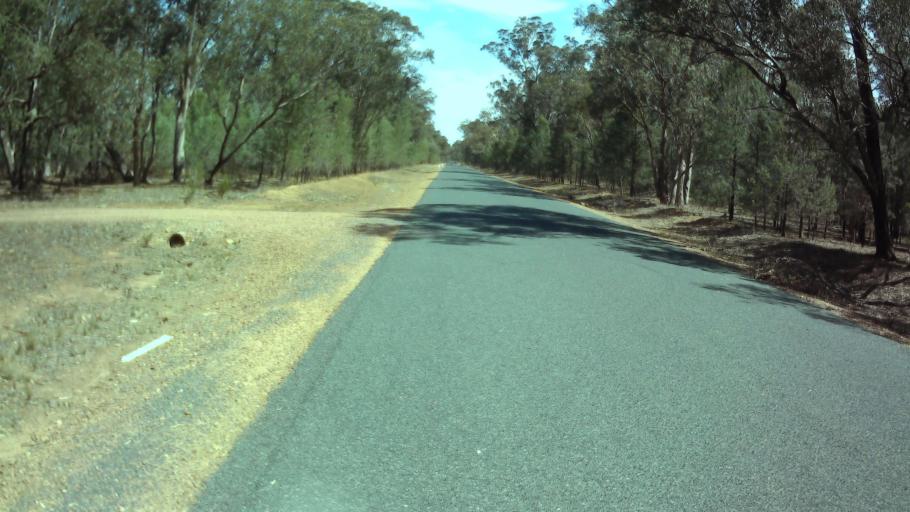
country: AU
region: New South Wales
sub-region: Weddin
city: Grenfell
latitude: -34.0314
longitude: 148.1335
